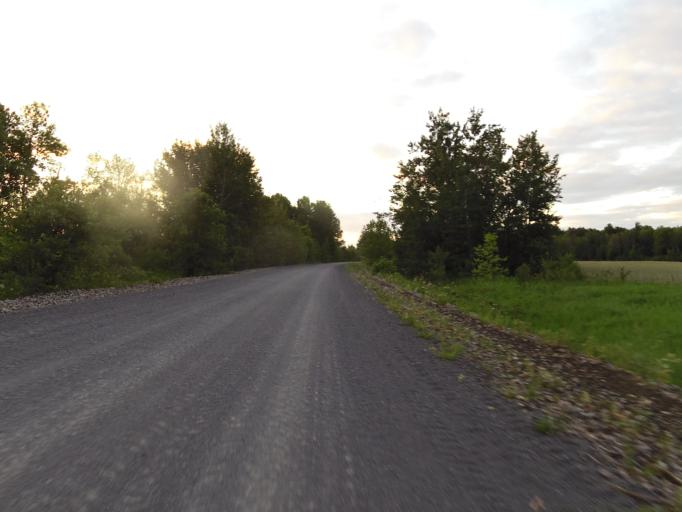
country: CA
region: Ontario
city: Arnprior
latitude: 45.3857
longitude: -76.3220
